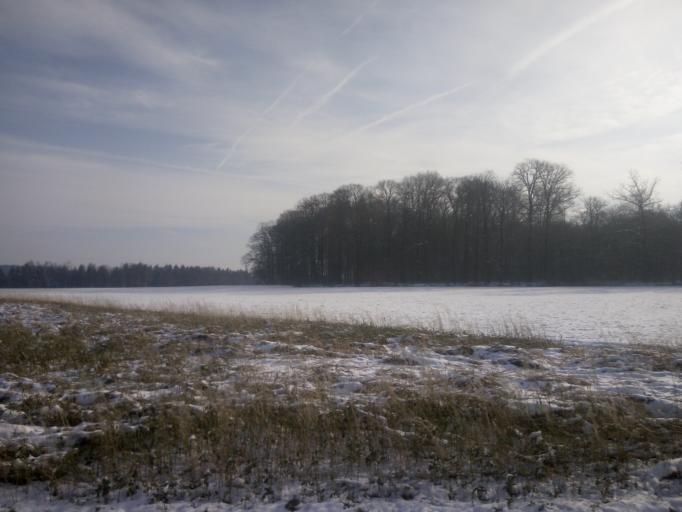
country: LU
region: Grevenmacher
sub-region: Canton d'Echternach
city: Consdorf
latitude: 49.7660
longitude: 6.3382
